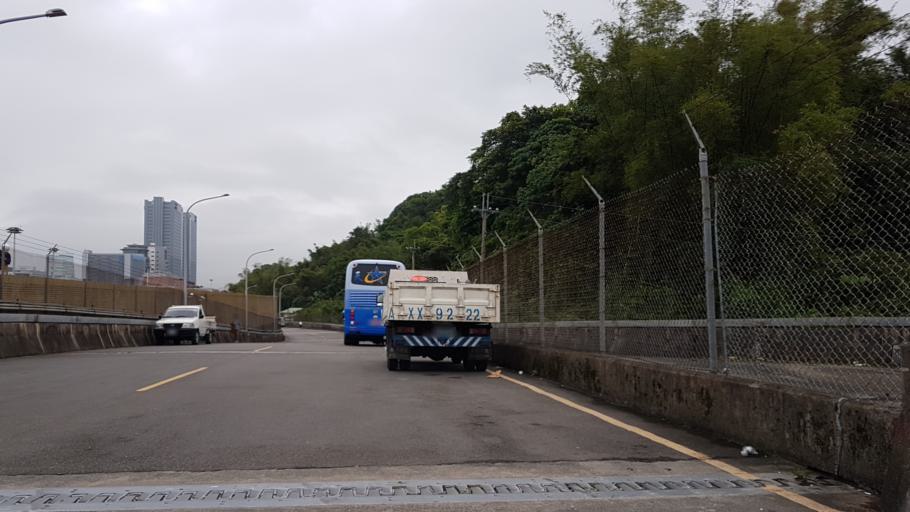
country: TW
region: Taipei
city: Taipei
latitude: 25.0496
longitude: 121.5972
